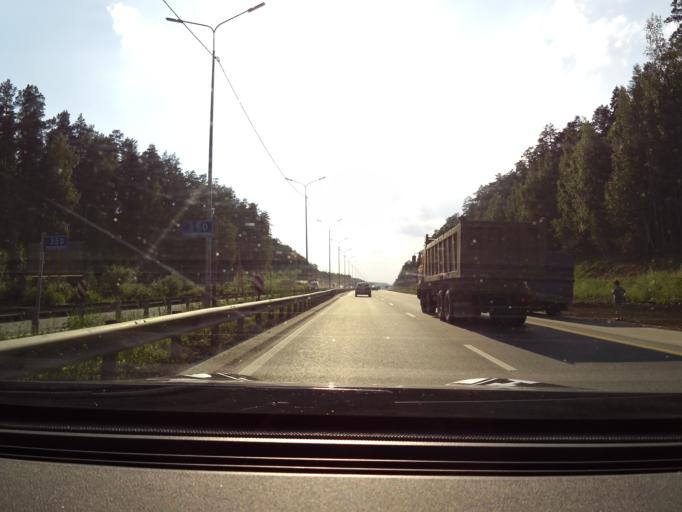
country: RU
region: Sverdlovsk
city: Shirokaya Rechka
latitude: 56.8258
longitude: 60.4528
